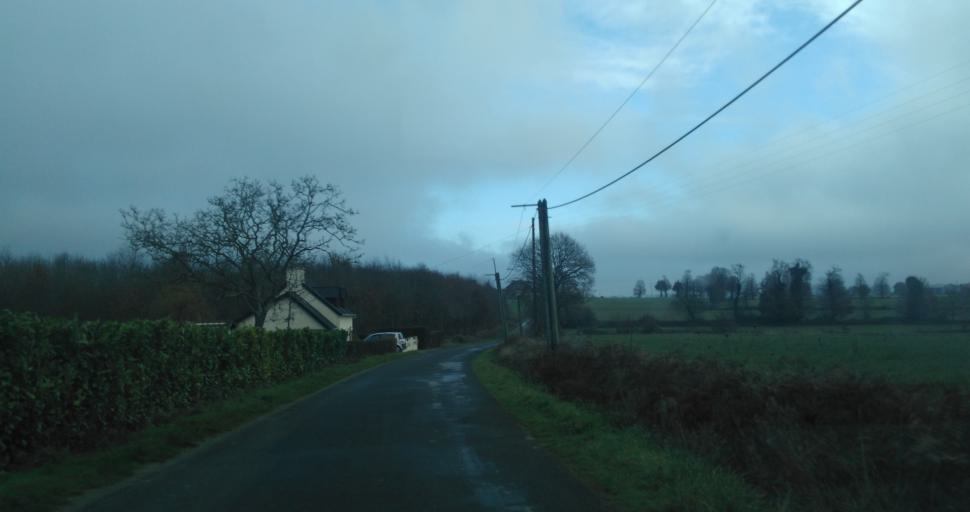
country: FR
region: Brittany
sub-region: Departement d'Ille-et-Vilaine
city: Boisgervilly
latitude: 48.1124
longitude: -2.1212
